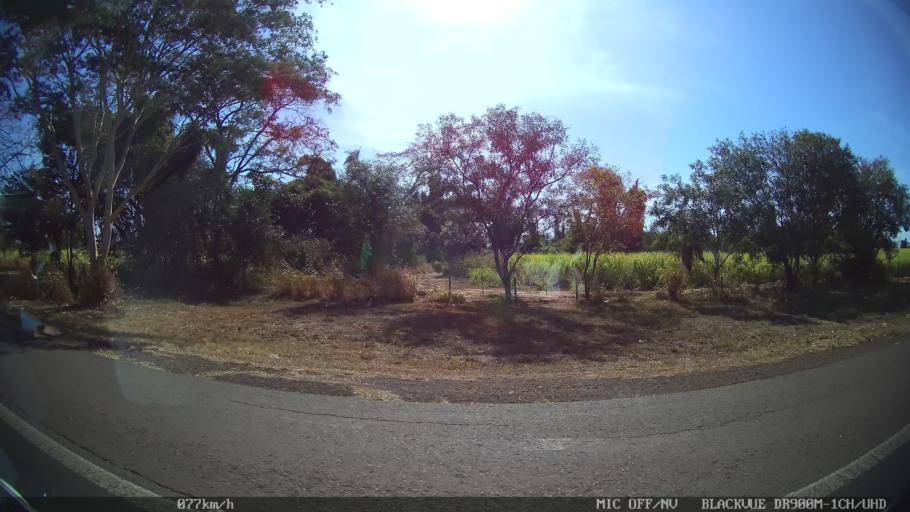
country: BR
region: Sao Paulo
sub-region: Barretos
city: Barretos
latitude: -20.5739
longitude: -48.6769
